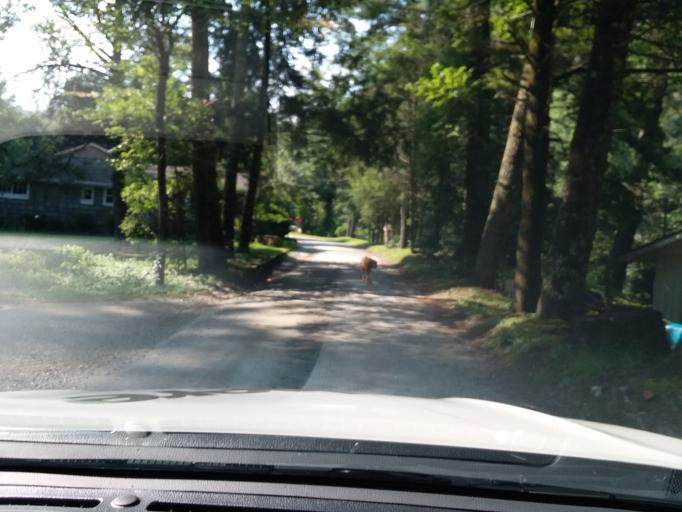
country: US
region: Georgia
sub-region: Habersham County
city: Clarkesville
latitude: 34.7553
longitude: -83.4961
